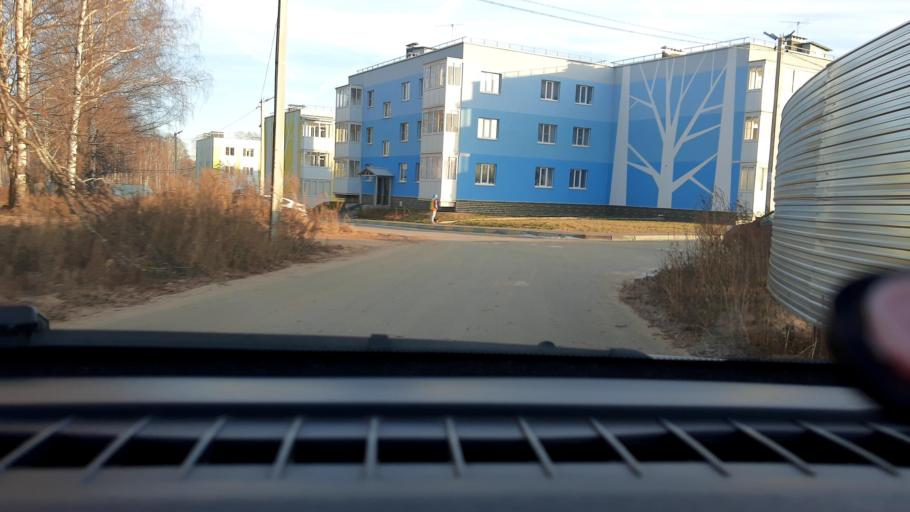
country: RU
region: Nizjnij Novgorod
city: Afonino
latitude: 56.2130
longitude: 44.0884
